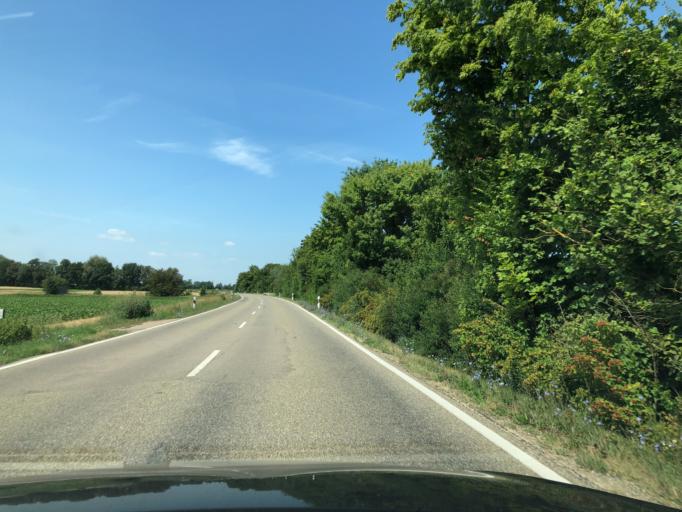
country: DE
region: Bavaria
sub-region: Swabia
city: Oberndorf
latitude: 48.6651
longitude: 10.8468
